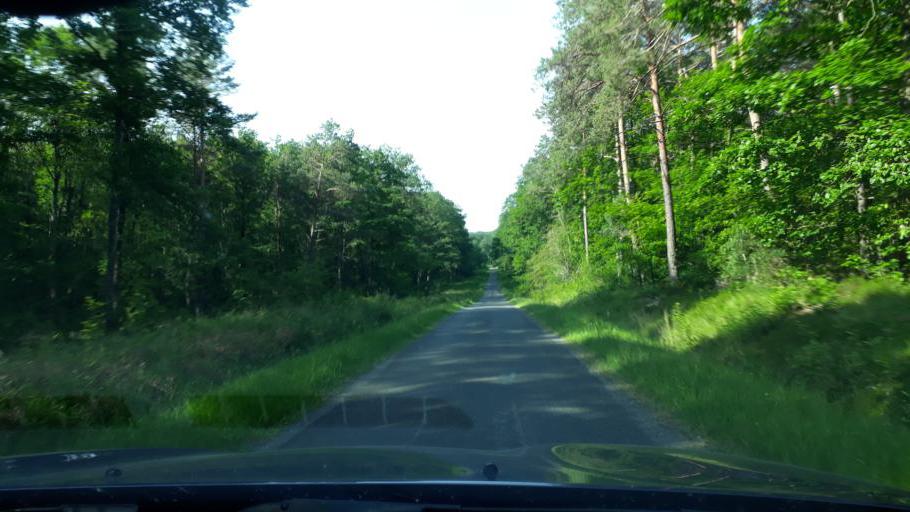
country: FR
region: Centre
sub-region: Departement du Loiret
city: Dadonville
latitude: 48.0502
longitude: 2.2715
